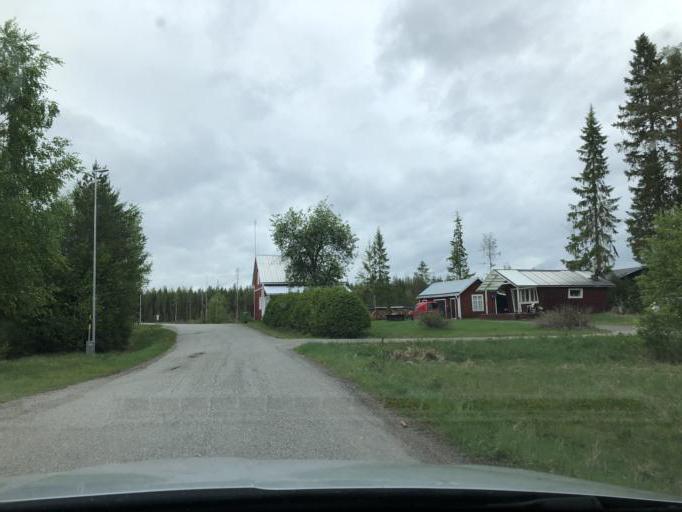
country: SE
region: Norrbotten
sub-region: Pitea Kommun
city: Roknas
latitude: 65.3779
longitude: 21.2779
